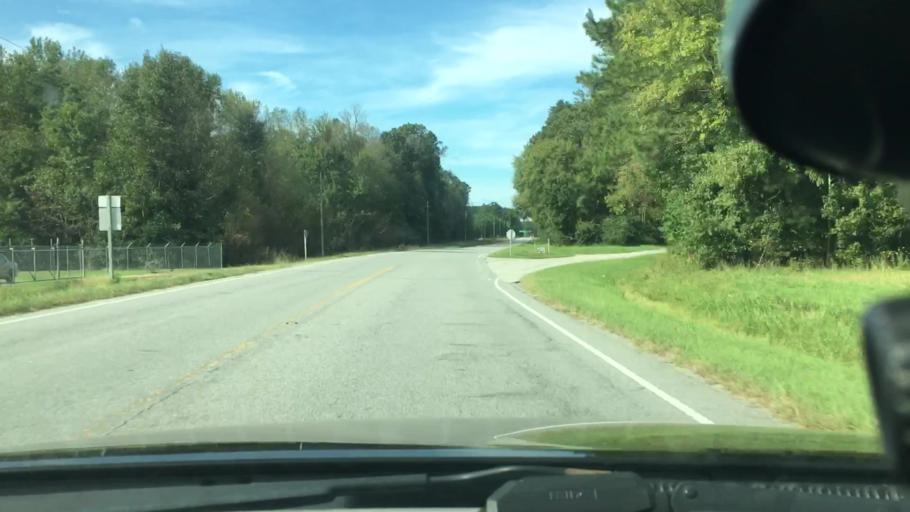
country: US
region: North Carolina
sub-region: Pitt County
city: Windsor
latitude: 35.4345
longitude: -77.2629
